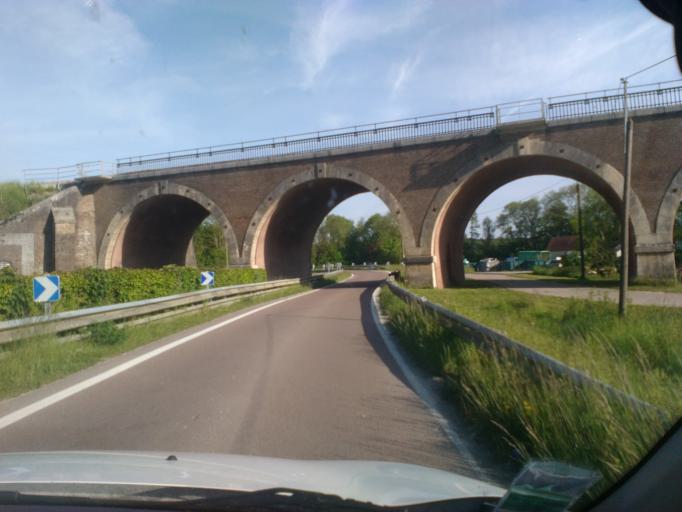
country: FR
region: Champagne-Ardenne
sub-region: Departement de l'Aube
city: Vendeuvre-sur-Barse
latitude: 48.2379
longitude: 4.4491
